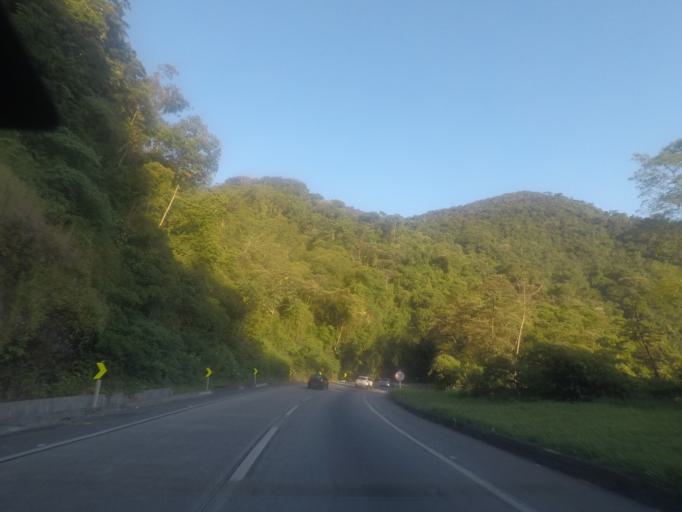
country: BR
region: Rio de Janeiro
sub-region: Petropolis
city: Petropolis
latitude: -22.5238
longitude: -43.2356
